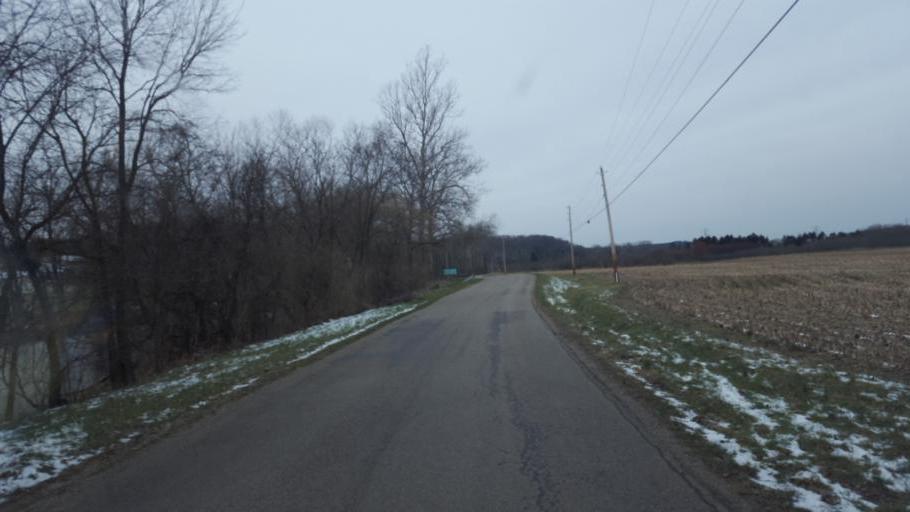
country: US
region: Ohio
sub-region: Sandusky County
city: Bellville
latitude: 40.5987
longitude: -82.4589
